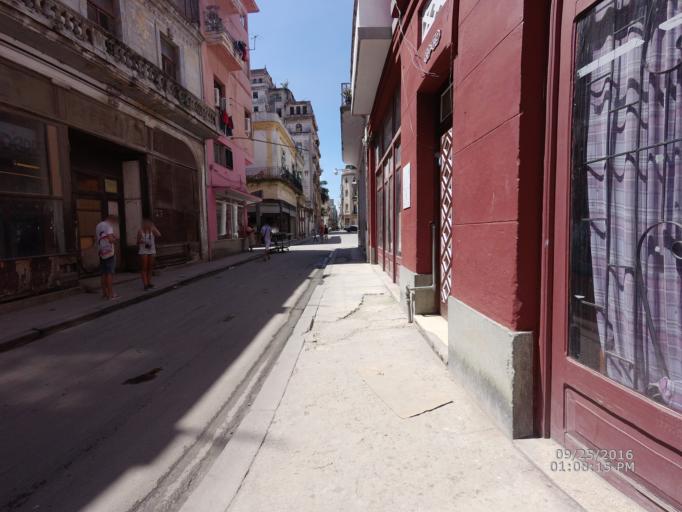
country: CU
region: La Habana
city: La Habana Vieja
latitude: 23.1391
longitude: -82.3534
